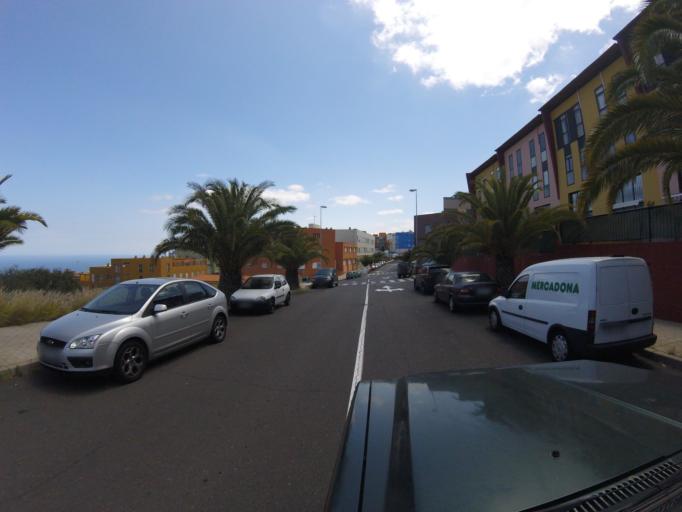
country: ES
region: Canary Islands
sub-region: Provincia de Santa Cruz de Tenerife
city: La Laguna
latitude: 28.4426
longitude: -16.3102
